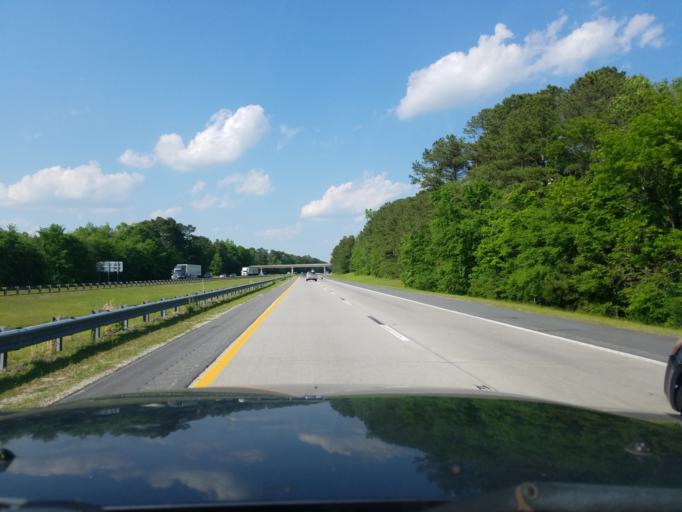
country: US
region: North Carolina
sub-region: Granville County
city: Creedmoor
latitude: 36.1689
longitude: -78.7074
